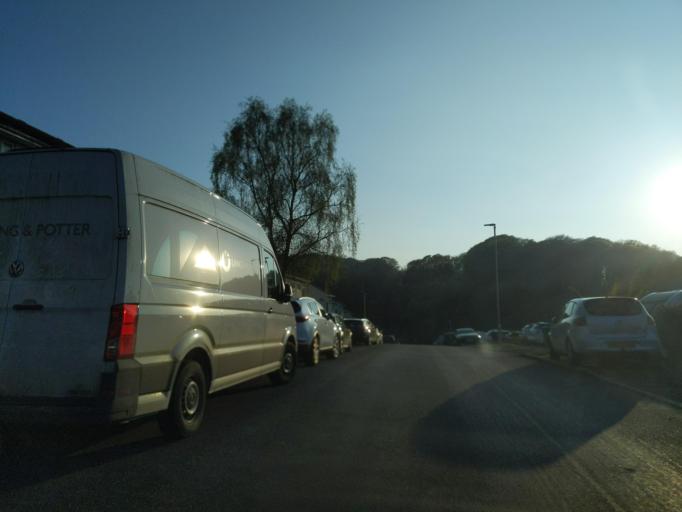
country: GB
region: England
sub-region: Plymouth
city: Plymstock
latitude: 50.3513
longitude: -4.0883
